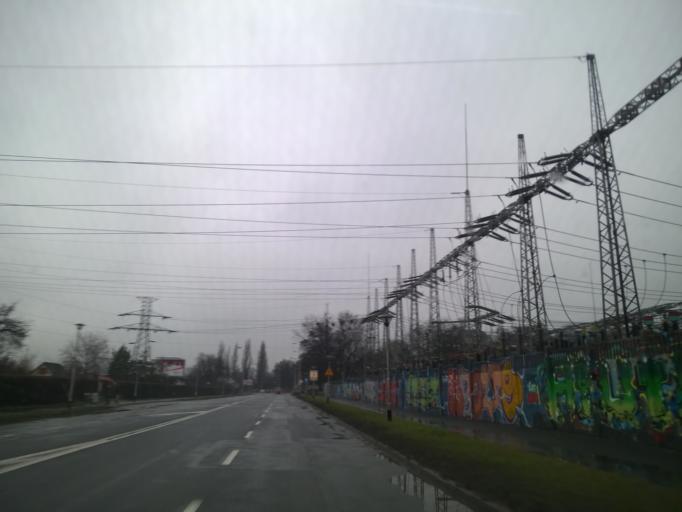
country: PL
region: Lower Silesian Voivodeship
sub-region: Powiat wroclawski
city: Wroclaw
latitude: 51.1235
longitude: 17.0113
